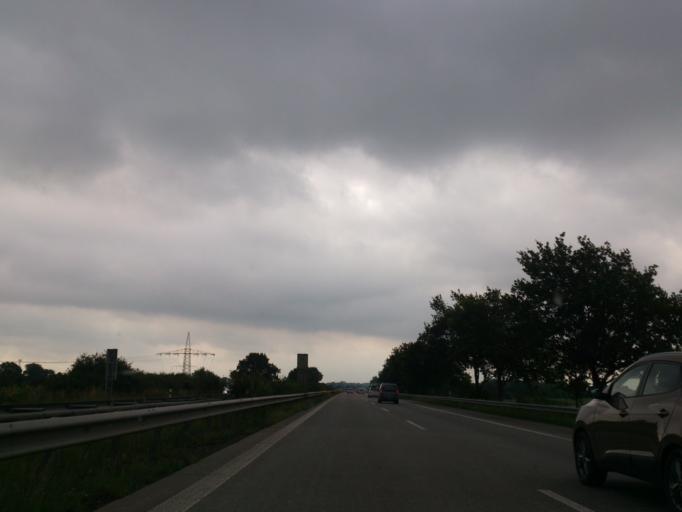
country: DE
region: Schleswig-Holstein
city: Hohenfelde
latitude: 53.8401
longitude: 9.6074
